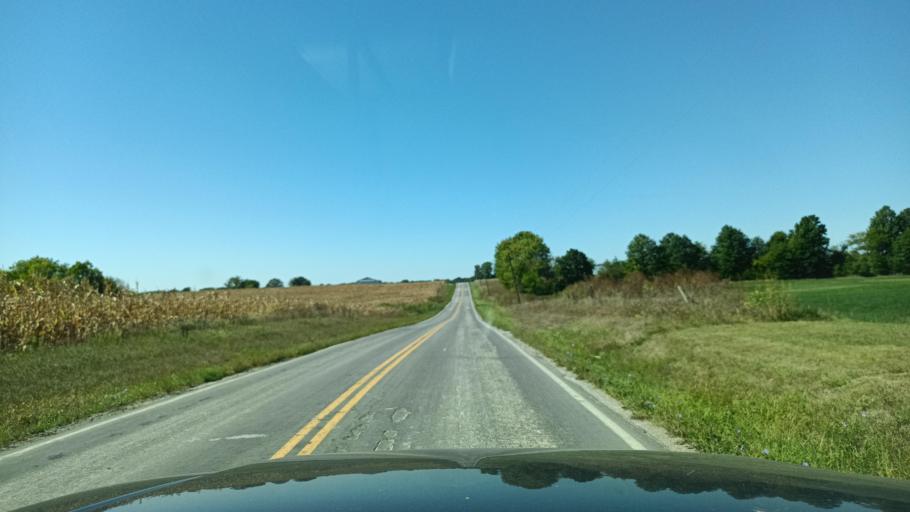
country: US
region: Missouri
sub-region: Macon County
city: La Plata
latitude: 40.0228
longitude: -92.5738
